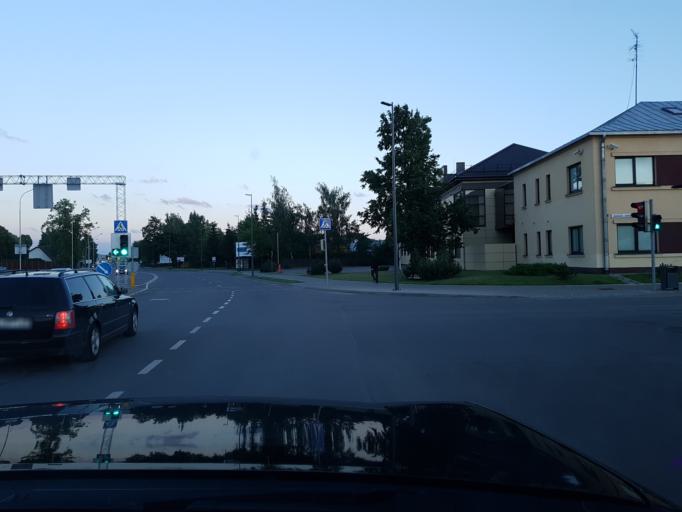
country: LT
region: Marijampoles apskritis
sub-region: Marijampole Municipality
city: Marijampole
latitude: 54.5608
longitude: 23.3531
